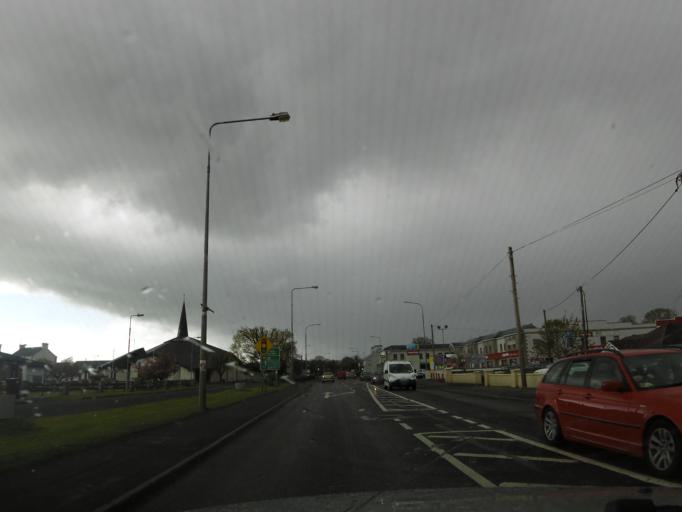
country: IE
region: Connaught
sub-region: County Galway
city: Claregalway
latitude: 53.3412
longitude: -8.9453
